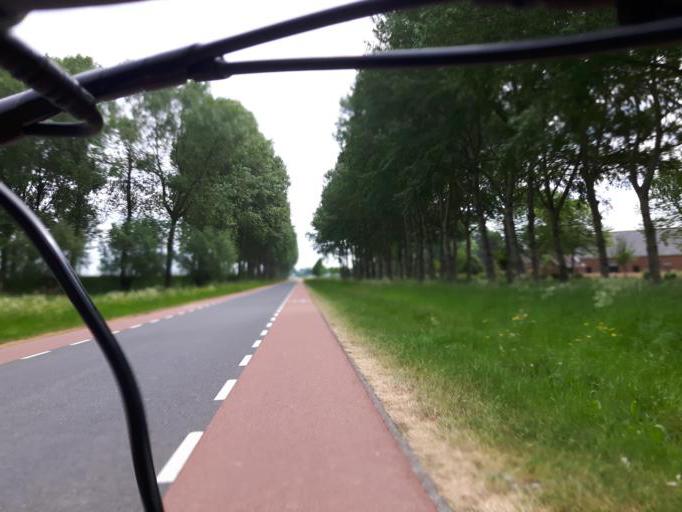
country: NL
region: Zeeland
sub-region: Gemeente Borsele
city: Borssele
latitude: 51.4410
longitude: 3.7792
